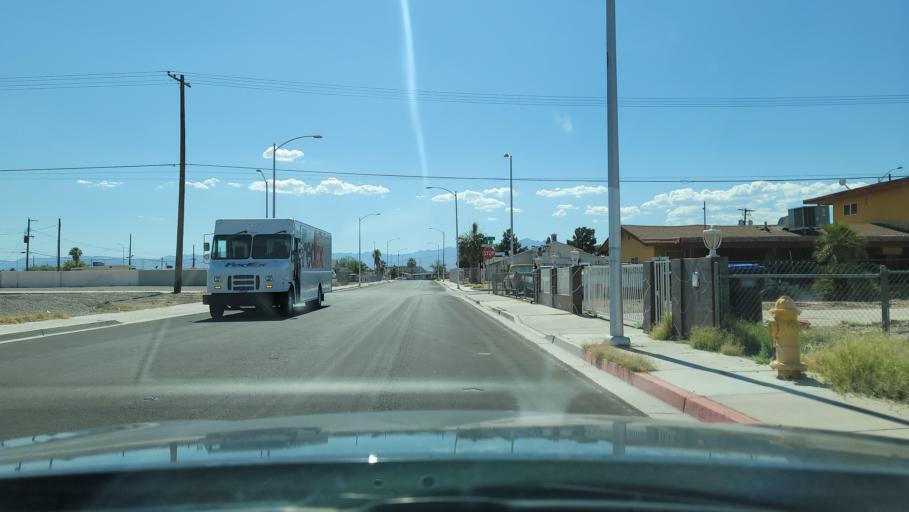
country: US
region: Nevada
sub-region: Clark County
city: Las Vegas
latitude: 36.1829
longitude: -115.1489
